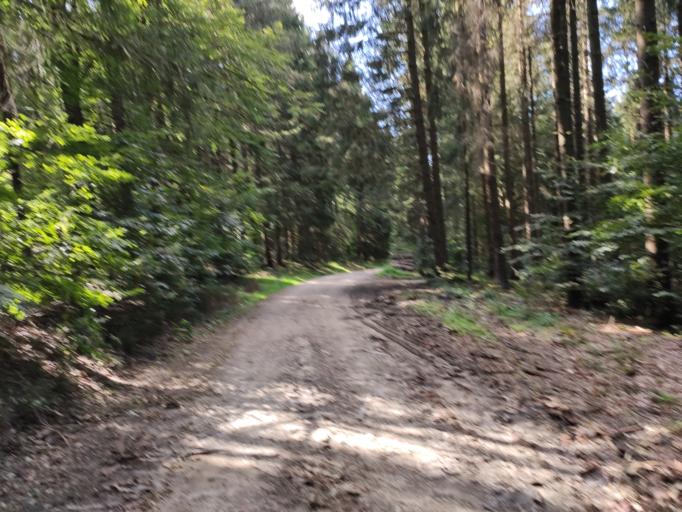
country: DE
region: Thuringia
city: Wurzbach
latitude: 50.4165
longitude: 11.5369
